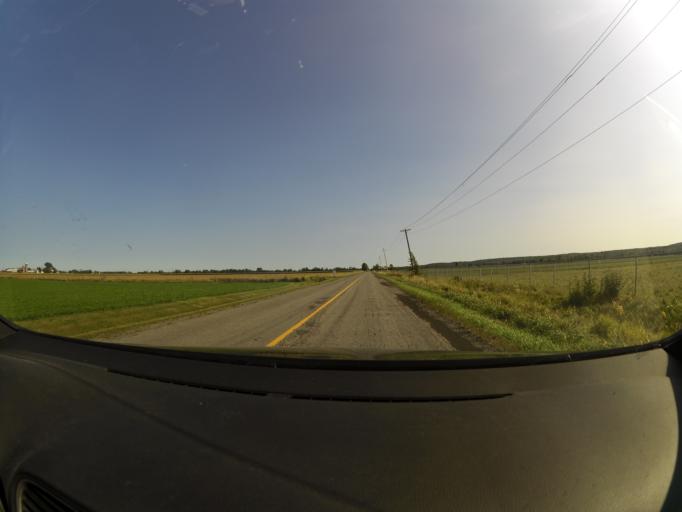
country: CA
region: Ontario
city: Arnprior
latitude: 45.3723
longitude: -76.3508
